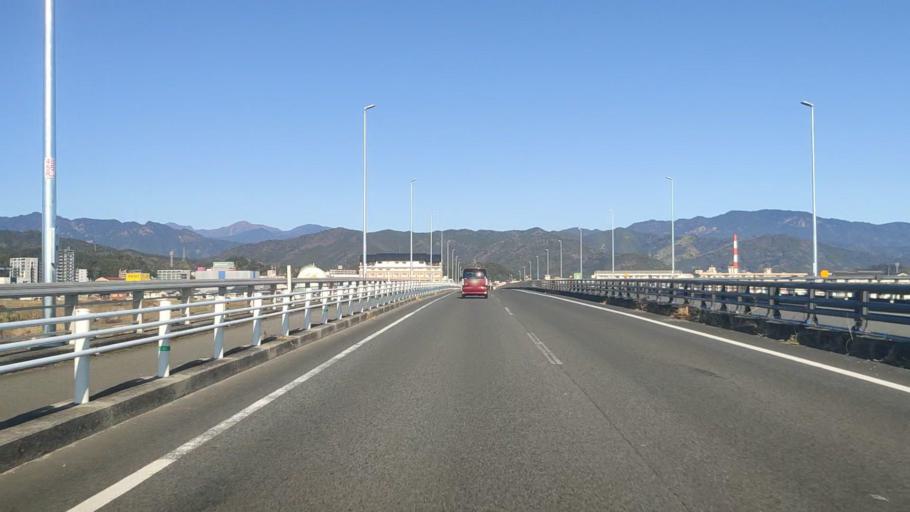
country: JP
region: Miyazaki
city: Nobeoka
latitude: 32.5824
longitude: 131.6803
